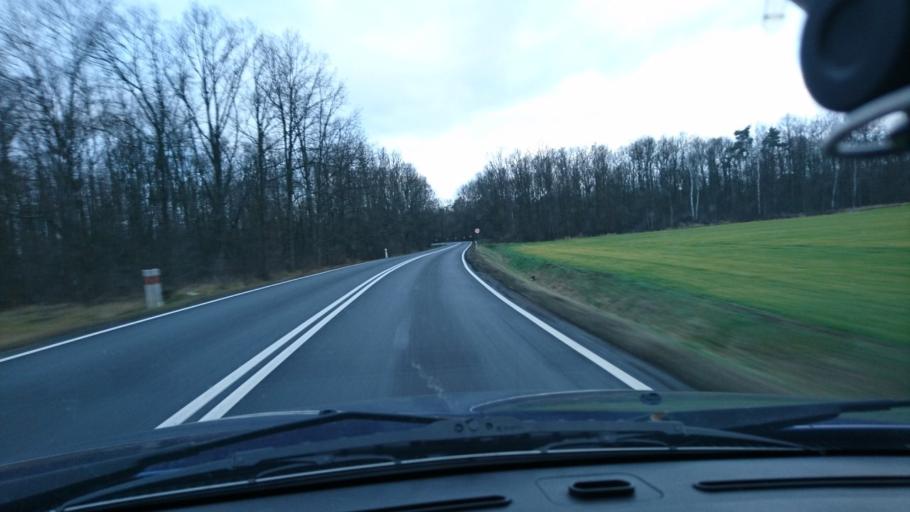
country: PL
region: Opole Voivodeship
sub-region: Powiat kluczborski
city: Byczyna
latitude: 51.1440
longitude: 18.1919
